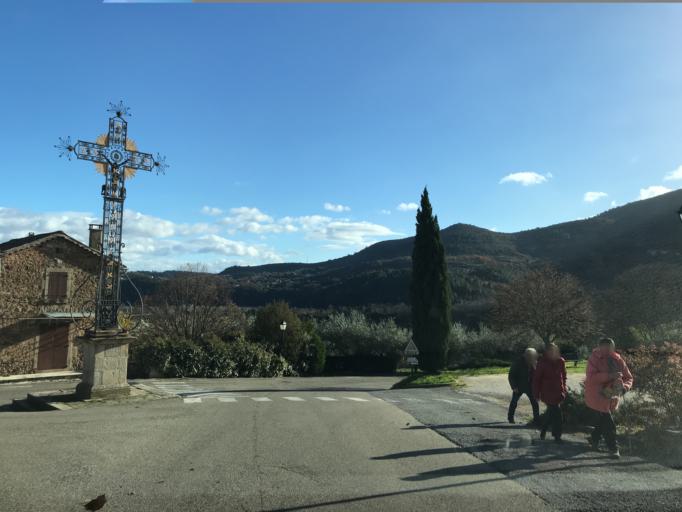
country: FR
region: Rhone-Alpes
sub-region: Departement de l'Ardeche
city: Les Vans
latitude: 44.4215
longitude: 4.0916
